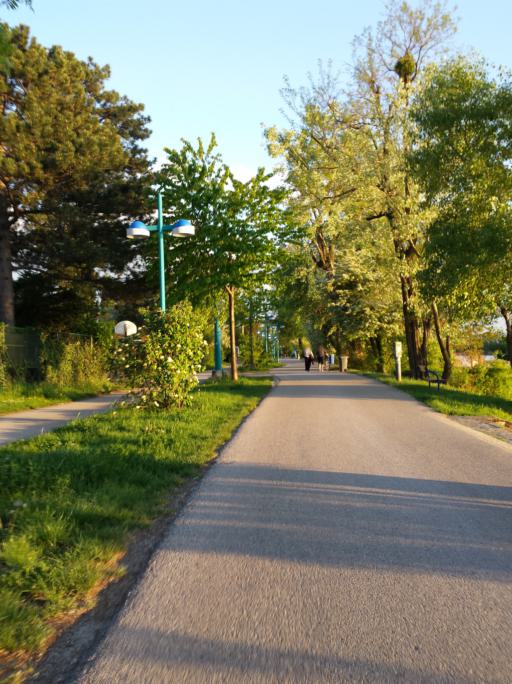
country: AT
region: Vienna
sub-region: Wien Stadt
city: Vienna
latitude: 48.2208
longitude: 16.4364
